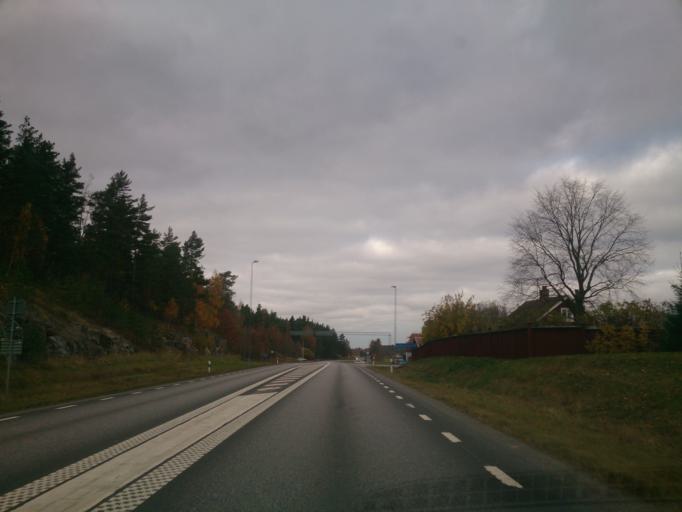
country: SE
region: OEstergoetland
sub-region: Linkopings Kommun
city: Linghem
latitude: 58.3557
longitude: 15.8319
